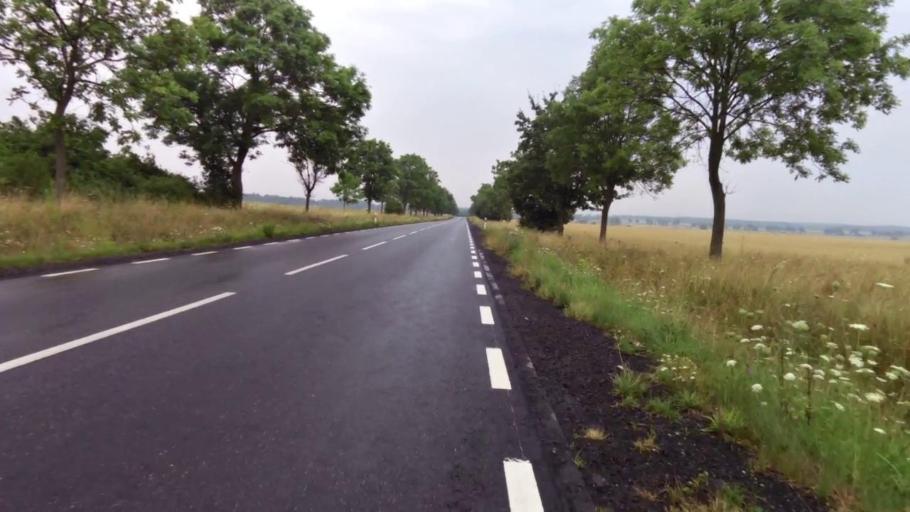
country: PL
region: West Pomeranian Voivodeship
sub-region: Powiat stargardzki
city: Insko
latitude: 53.4563
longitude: 15.5801
